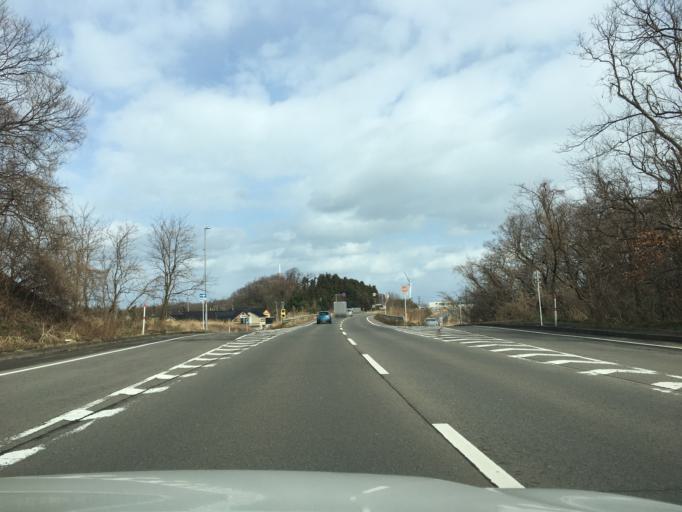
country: JP
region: Yamagata
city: Yuza
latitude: 39.2638
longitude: 139.9238
